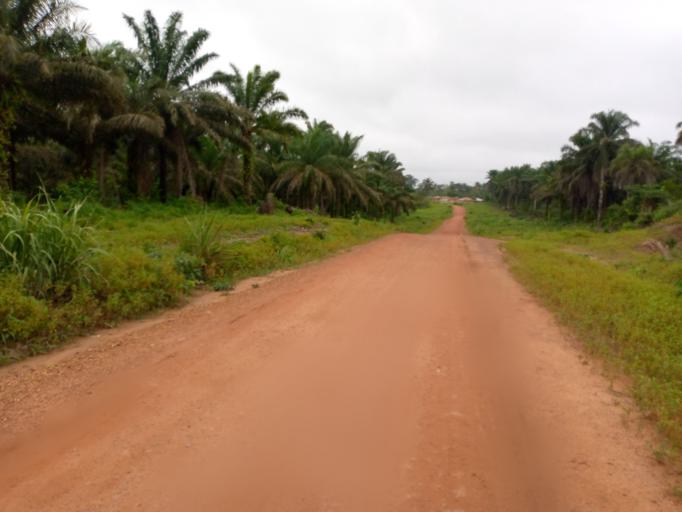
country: SL
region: Southern Province
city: Sumbuya
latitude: 7.5997
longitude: -12.0835
